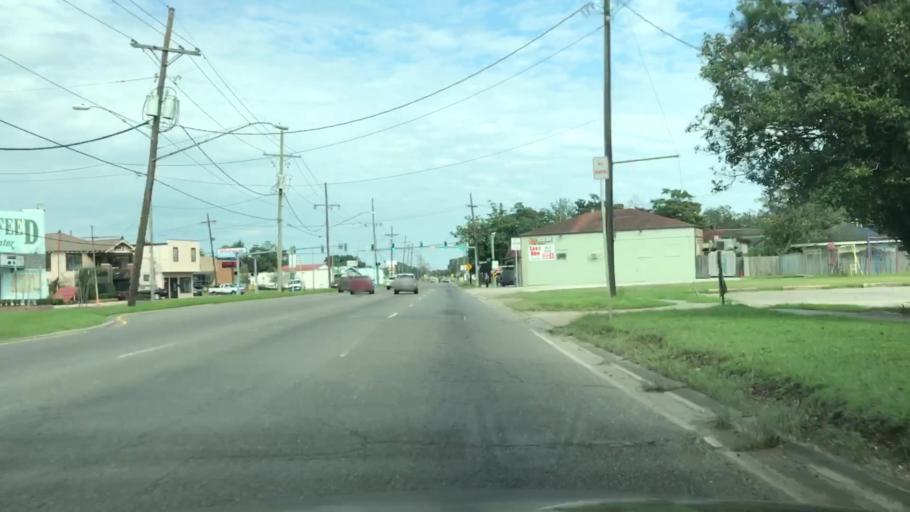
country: US
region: Louisiana
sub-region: Jefferson Parish
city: Elmwood
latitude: 29.9590
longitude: -90.1728
